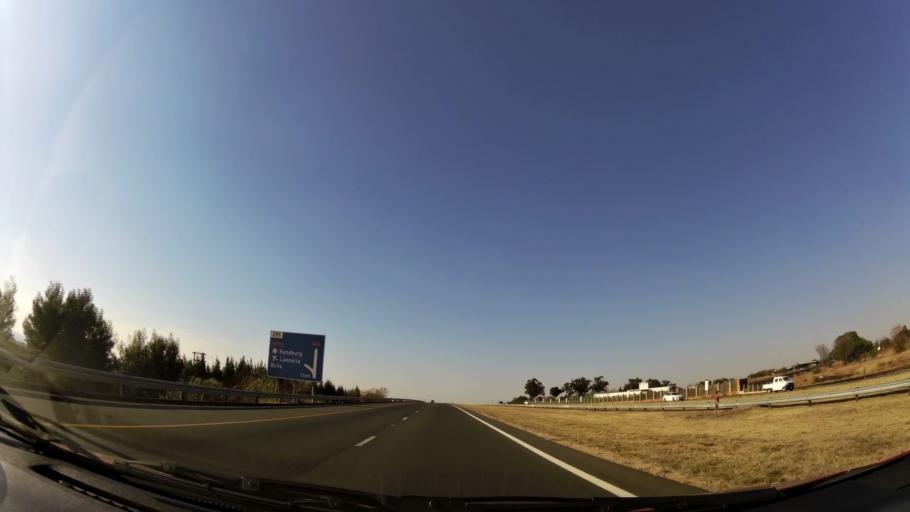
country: ZA
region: Gauteng
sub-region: West Rand District Municipality
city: Muldersdriseloop
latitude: -25.9927
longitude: 27.9127
